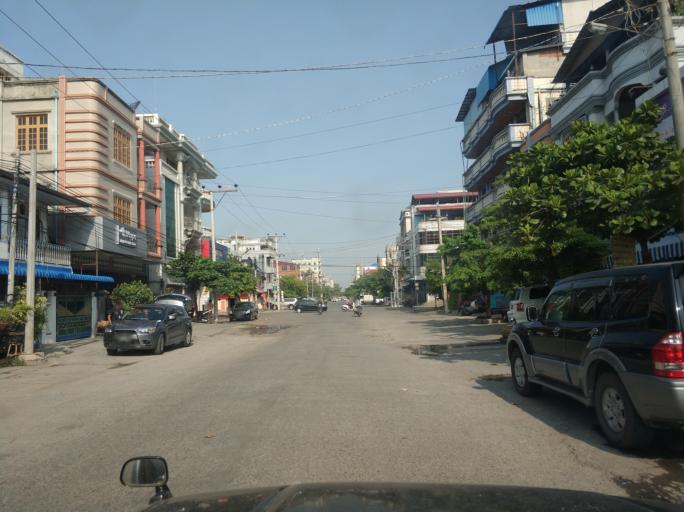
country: MM
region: Mandalay
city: Mandalay
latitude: 21.9704
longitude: 96.0935
